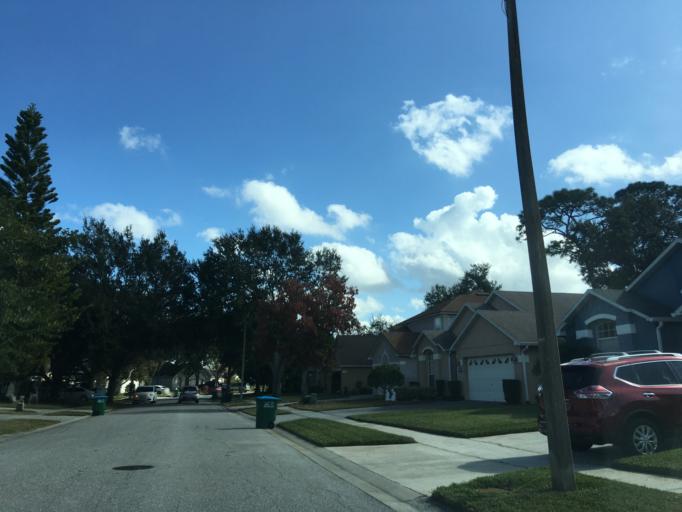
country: US
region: Florida
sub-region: Orange County
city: Eatonville
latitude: 28.6278
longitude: -81.4075
